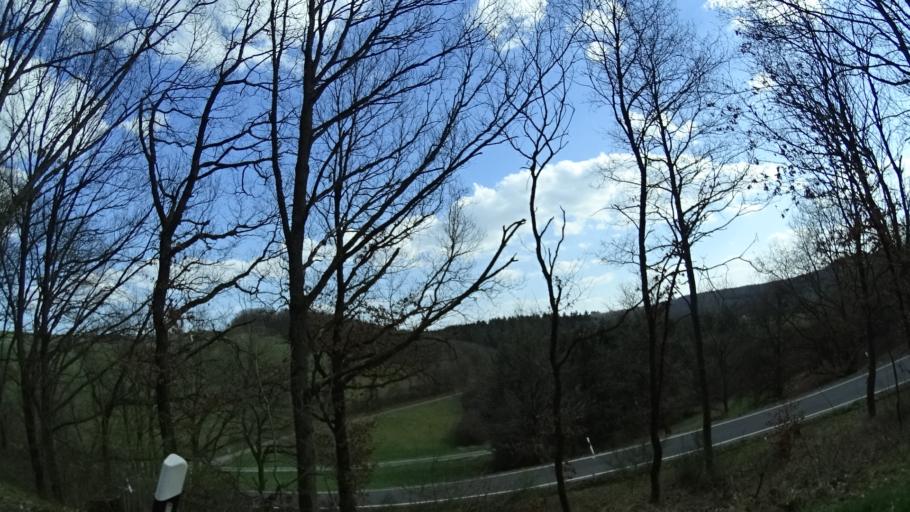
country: DE
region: Rheinland-Pfalz
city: Schmidthachenbach
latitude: 49.7352
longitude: 7.4755
